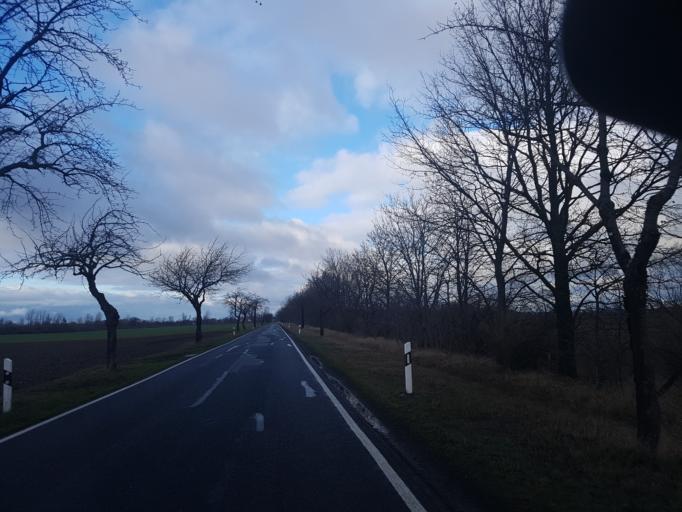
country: DE
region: Brandenburg
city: Muhlberg
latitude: 51.4210
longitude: 13.2309
